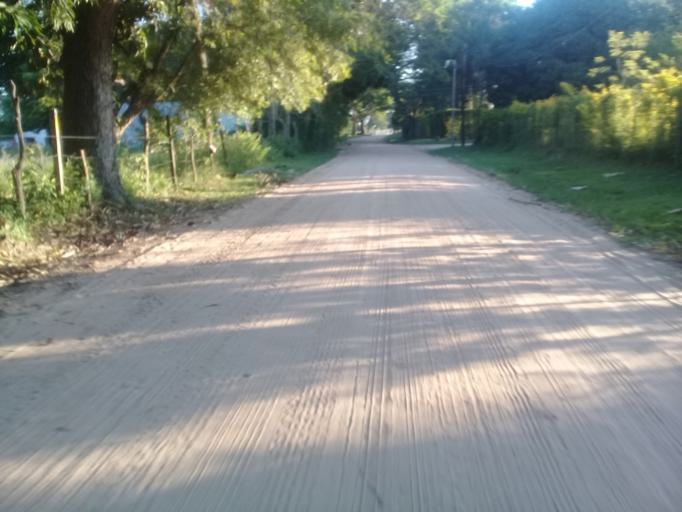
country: AR
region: Corrientes
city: San Luis del Palmar
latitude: -27.4650
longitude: -58.6620
